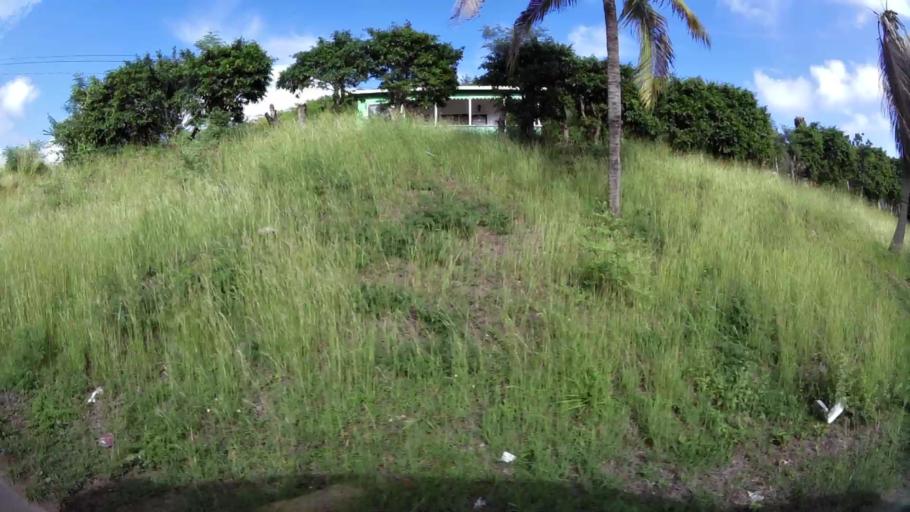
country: AG
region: Saint Paul
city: Liberta
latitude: 17.0309
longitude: -61.7877
